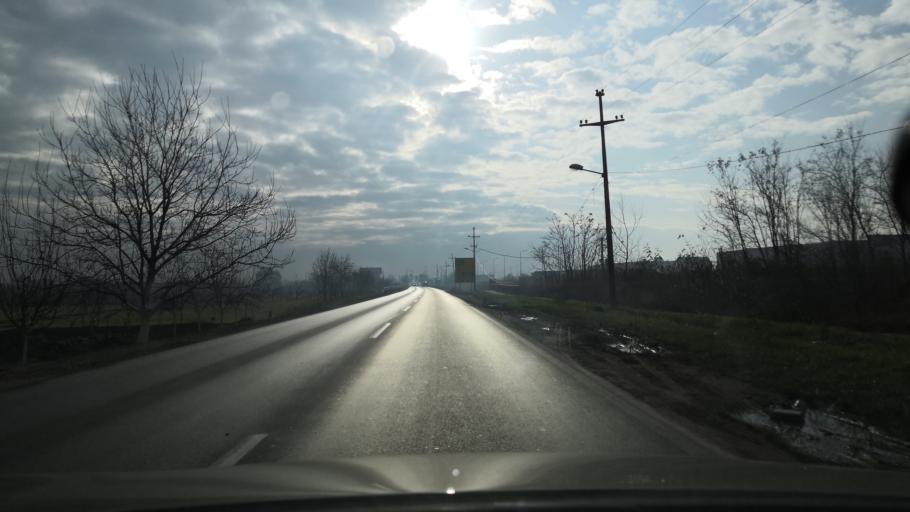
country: RS
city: Dobanovci
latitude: 44.8512
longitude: 20.2069
